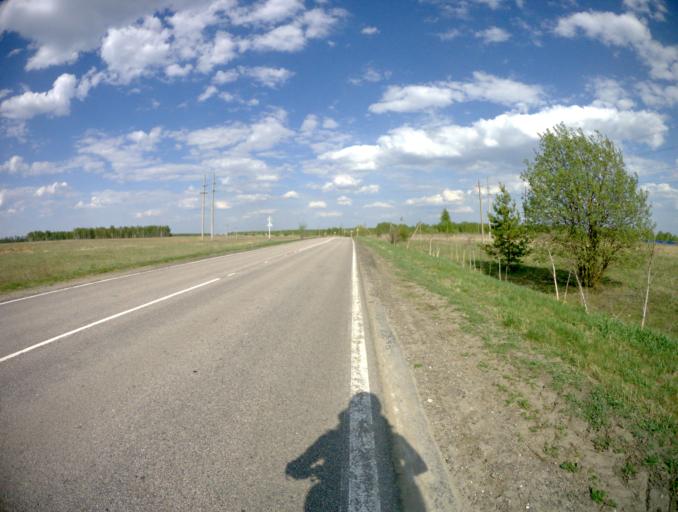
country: RU
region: Vladimir
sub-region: Kovrovskiy Rayon
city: Kovrov
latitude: 56.4515
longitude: 41.3334
